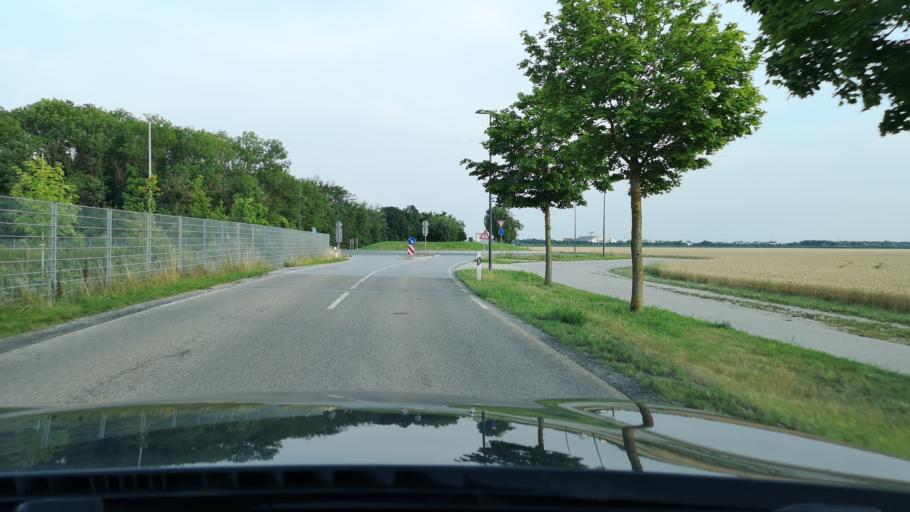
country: DE
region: Bavaria
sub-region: Upper Bavaria
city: Kirchheim bei Muenchen
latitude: 48.1611
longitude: 11.7840
